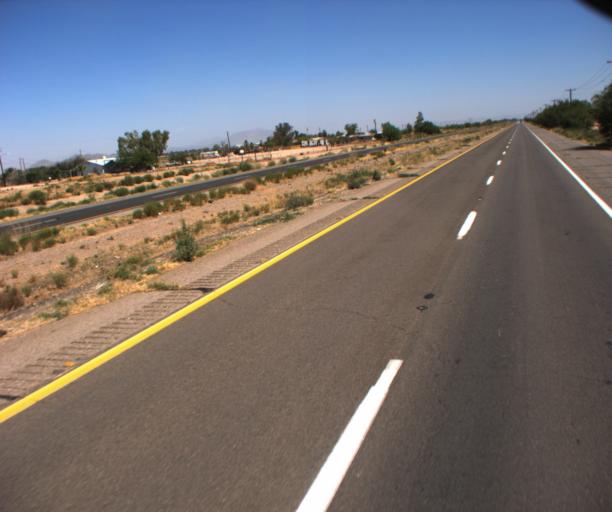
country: US
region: Arizona
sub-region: Pinal County
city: Maricopa
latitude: 32.9025
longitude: -112.0493
